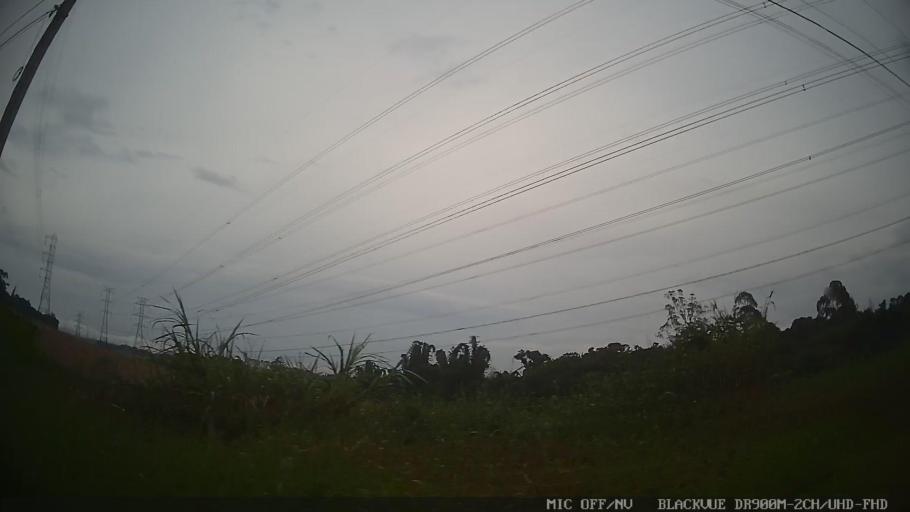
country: BR
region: Sao Paulo
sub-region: Suzano
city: Suzano
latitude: -23.6709
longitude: -46.2369
